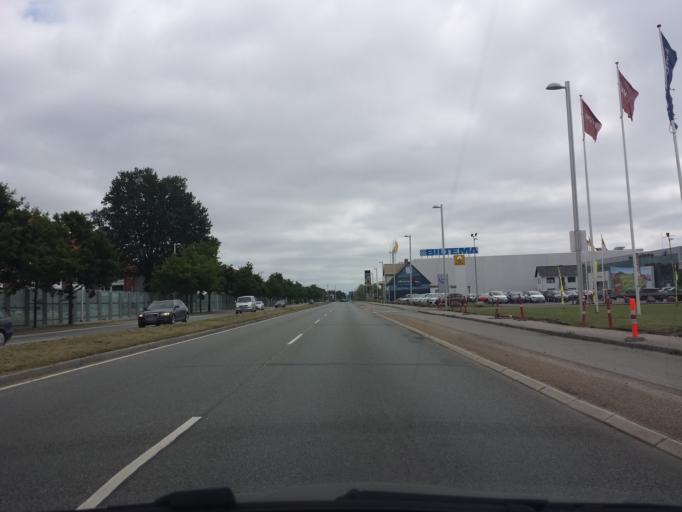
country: DK
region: Capital Region
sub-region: Albertslund Kommune
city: Albertslund
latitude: 55.6641
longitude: 12.3742
